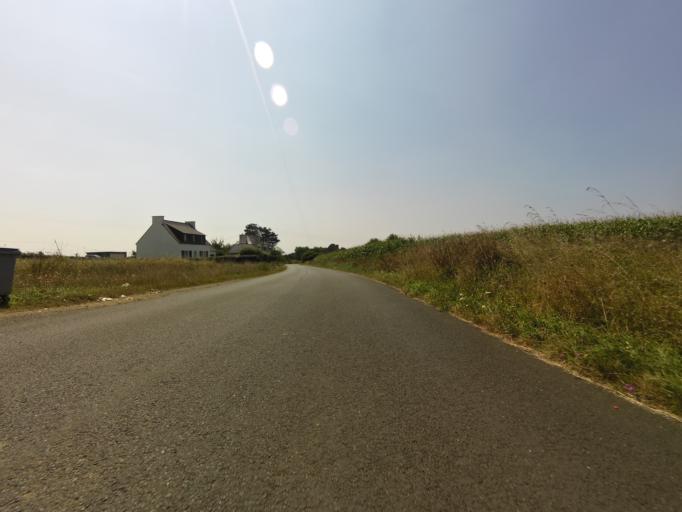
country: FR
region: Brittany
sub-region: Departement du Finistere
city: Pouldreuzic
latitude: 47.9064
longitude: -4.3534
